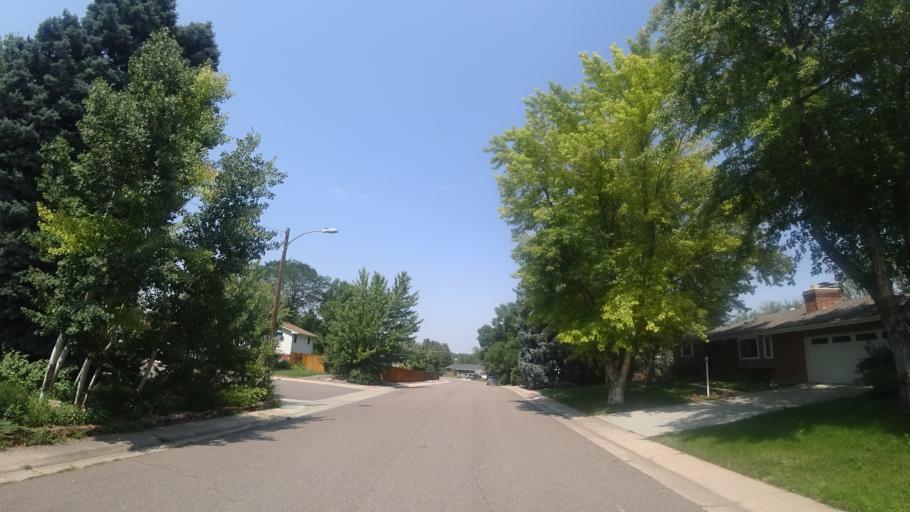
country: US
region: Colorado
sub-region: Arapahoe County
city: Greenwood Village
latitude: 39.6108
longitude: -104.9813
